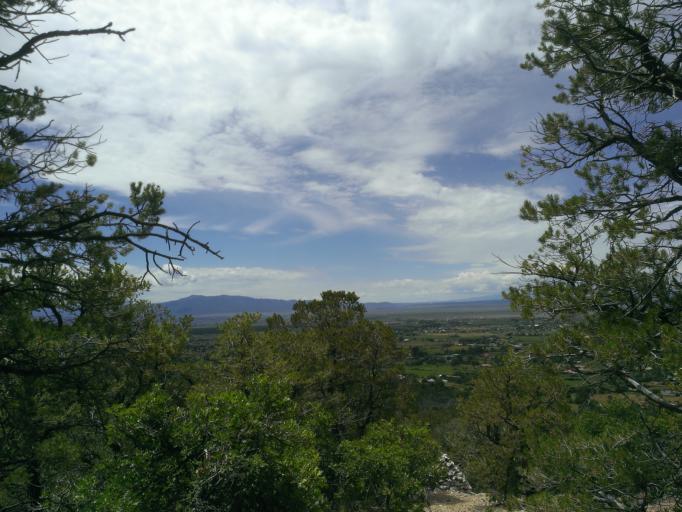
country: US
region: New Mexico
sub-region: Taos County
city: Arroyo Seco
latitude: 36.5369
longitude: -105.5549
